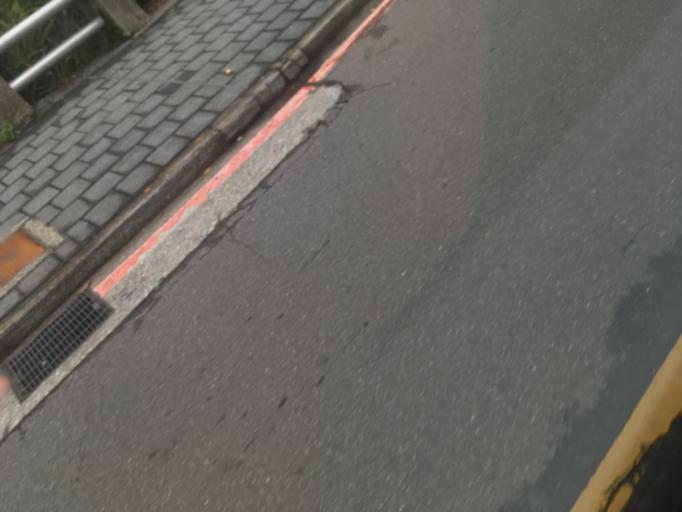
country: TW
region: Taipei
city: Taipei
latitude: 25.1442
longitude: 121.5269
